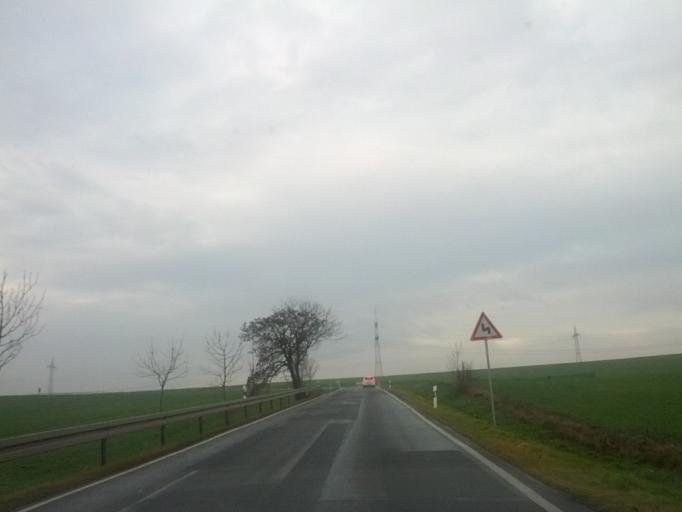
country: DE
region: Thuringia
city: Friedrichswerth
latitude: 50.9830
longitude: 10.5470
